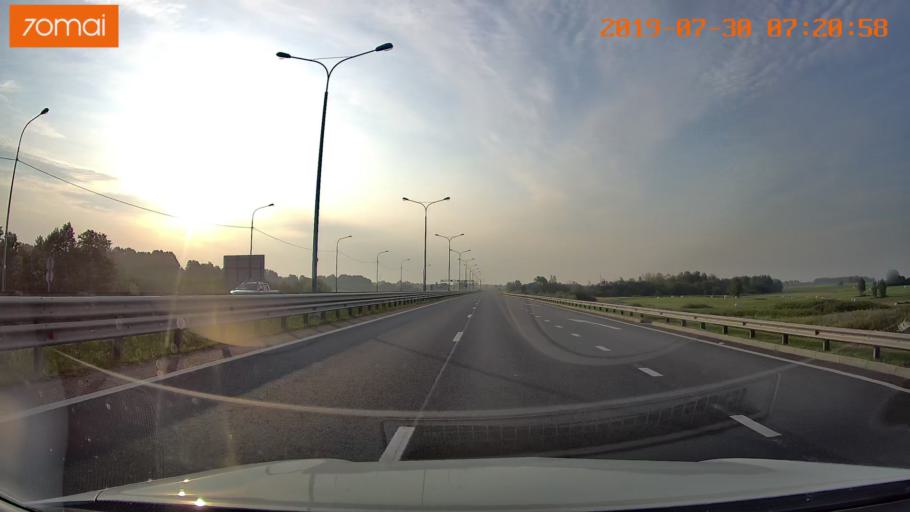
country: RU
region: Kaliningrad
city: Bol'shoe Isakovo
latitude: 54.6986
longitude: 20.7158
